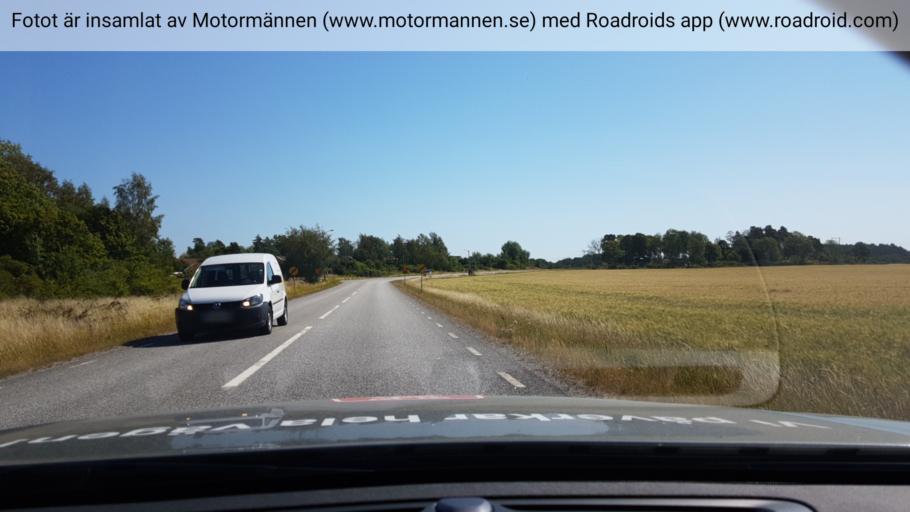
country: SE
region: Stockholm
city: Stenhamra
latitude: 59.3986
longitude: 17.5610
